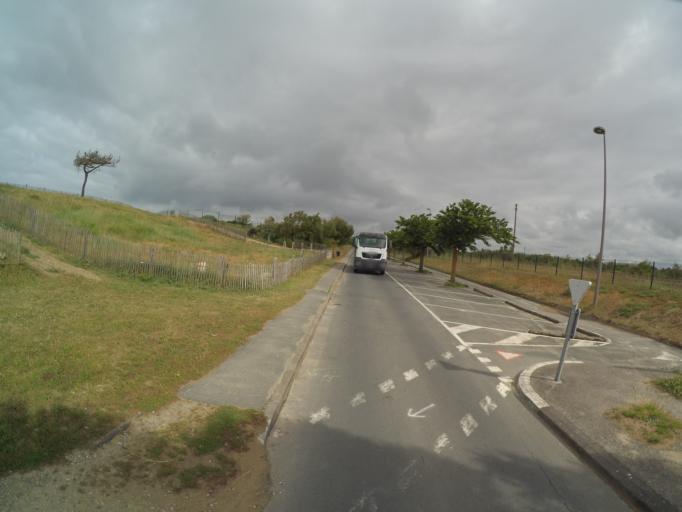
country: FR
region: Poitou-Charentes
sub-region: Departement de la Charente-Maritime
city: Aytre
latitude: 46.1230
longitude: -1.1251
